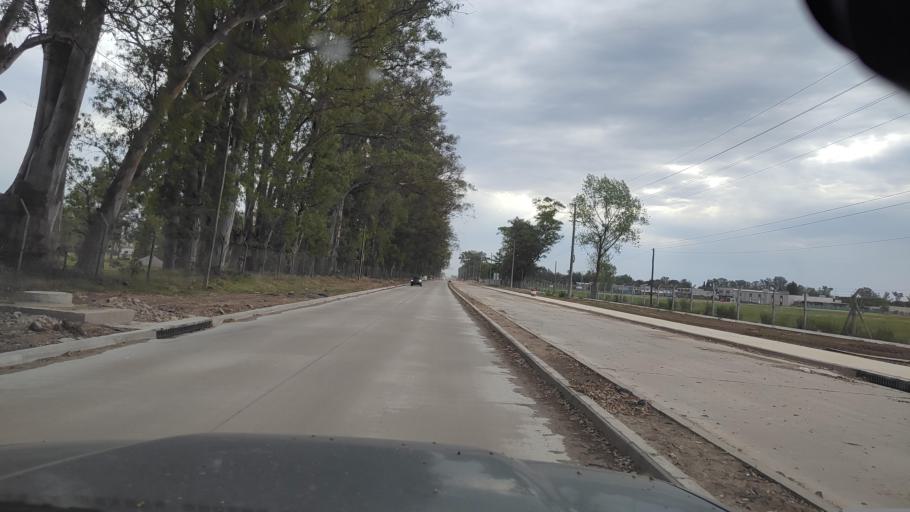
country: AR
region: Buenos Aires
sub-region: Partido de Lujan
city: Lujan
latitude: -34.5508
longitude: -59.0883
